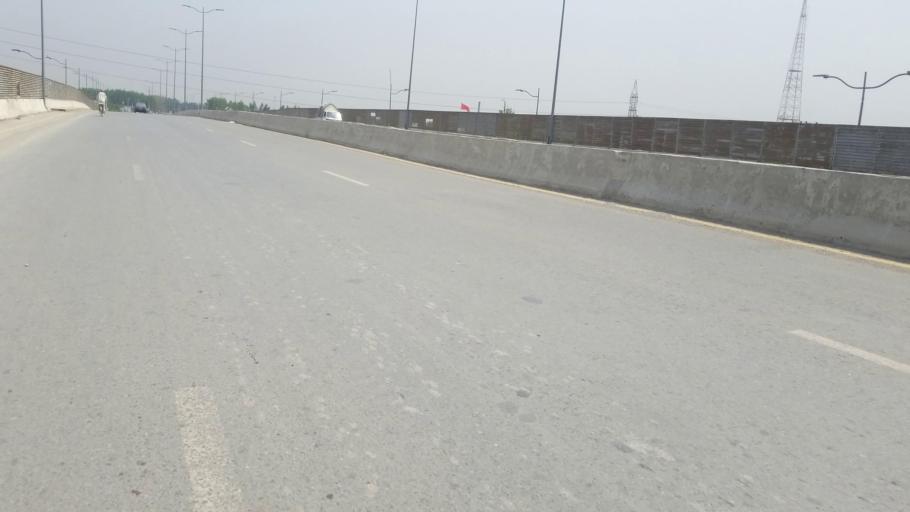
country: PK
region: Khyber Pakhtunkhwa
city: Peshawar
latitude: 34.0312
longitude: 71.5541
